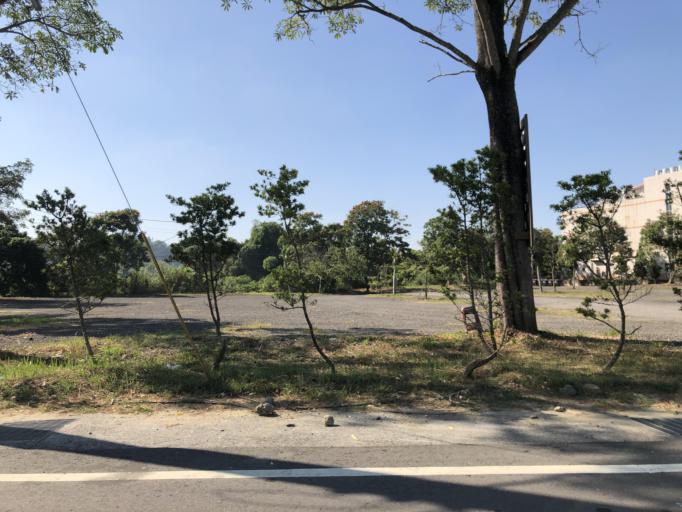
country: TW
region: Taiwan
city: Yujing
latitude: 23.0622
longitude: 120.3901
